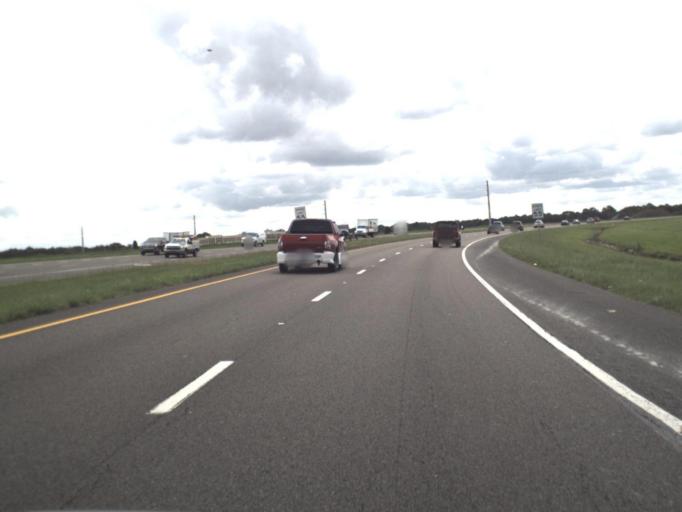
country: US
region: Florida
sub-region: Manatee County
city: Samoset
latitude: 27.4649
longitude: -82.5316
